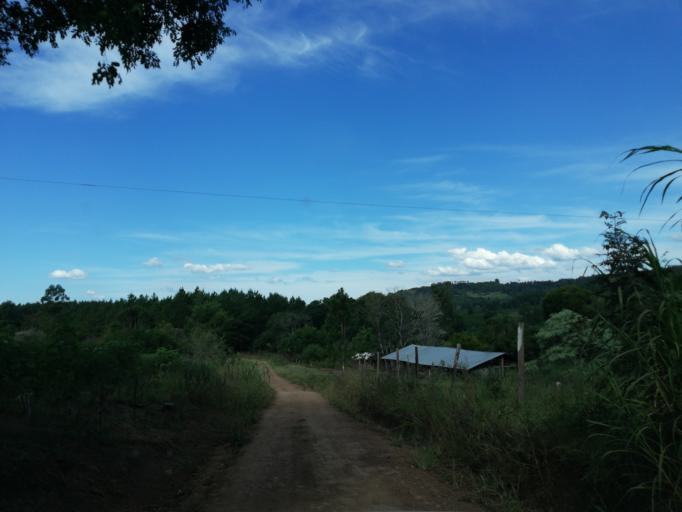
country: AR
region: Misiones
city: Dos de Mayo
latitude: -27.0162
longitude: -54.4232
